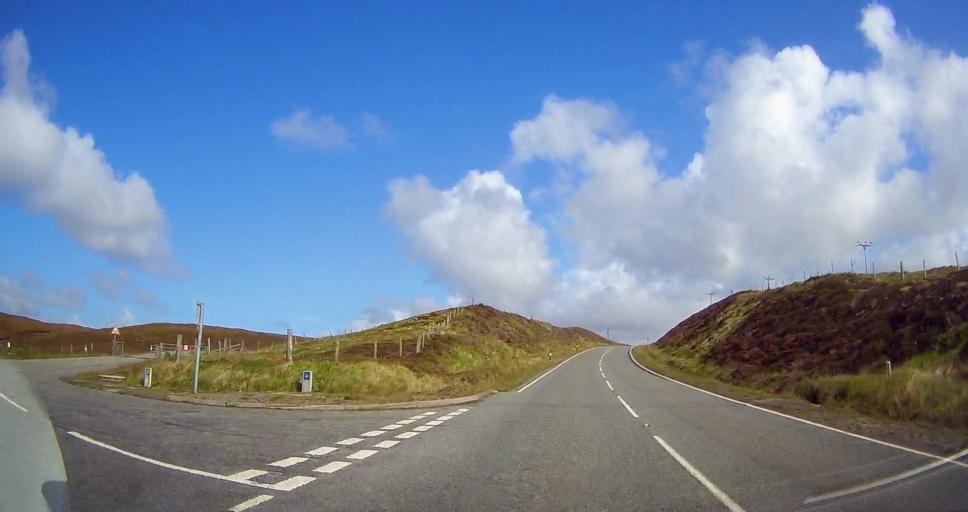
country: GB
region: Scotland
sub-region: Shetland Islands
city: Lerwick
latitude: 60.4666
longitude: -1.4065
